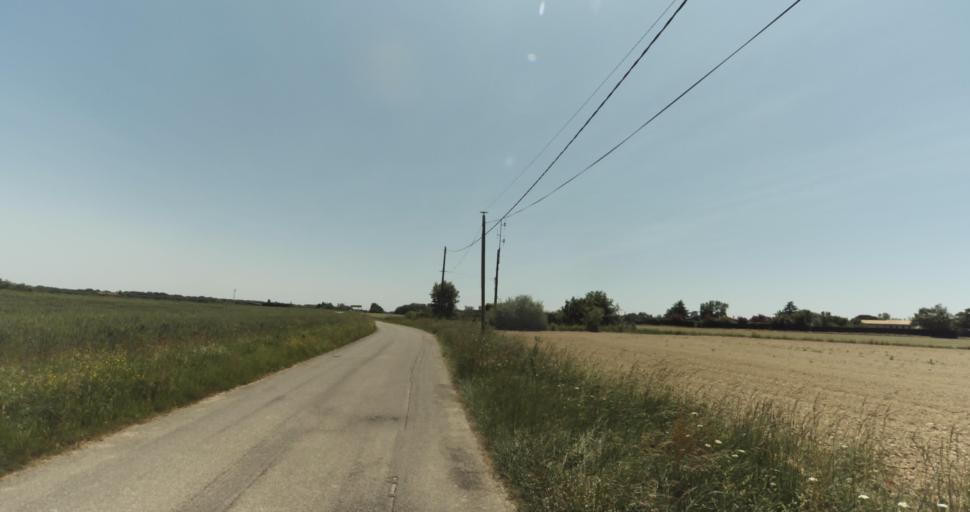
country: FR
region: Midi-Pyrenees
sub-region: Departement de la Haute-Garonne
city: Levignac
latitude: 43.6473
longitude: 1.1903
